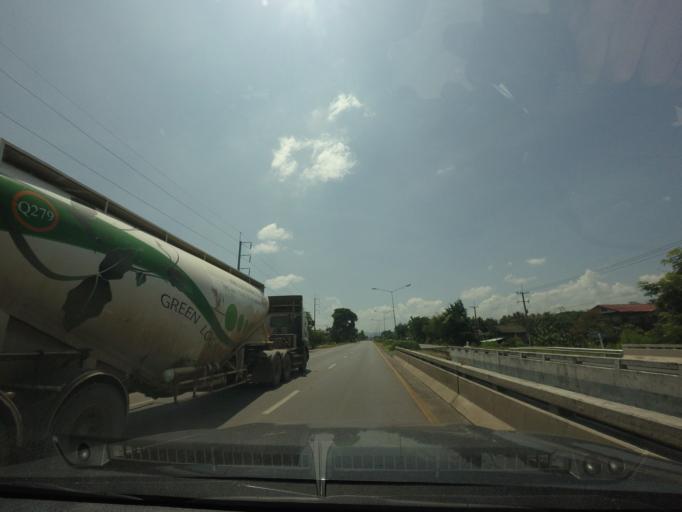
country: TH
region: Phetchabun
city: Lom Sak
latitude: 16.7105
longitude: 101.1780
